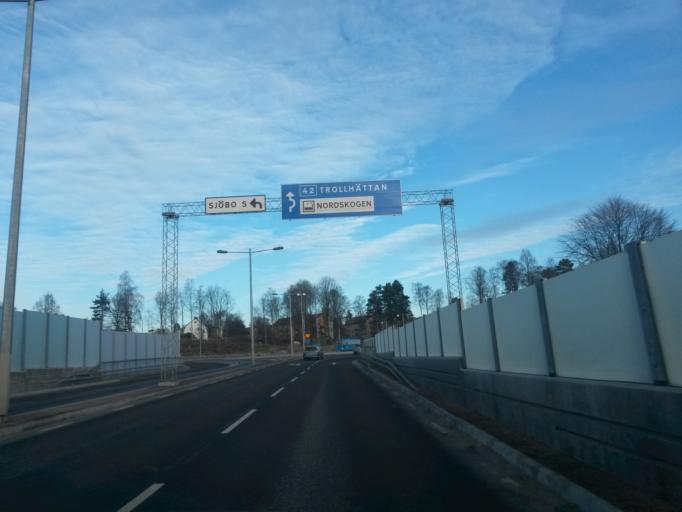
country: SE
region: Vaestra Goetaland
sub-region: Boras Kommun
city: Boras
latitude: 57.7406
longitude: 12.9387
